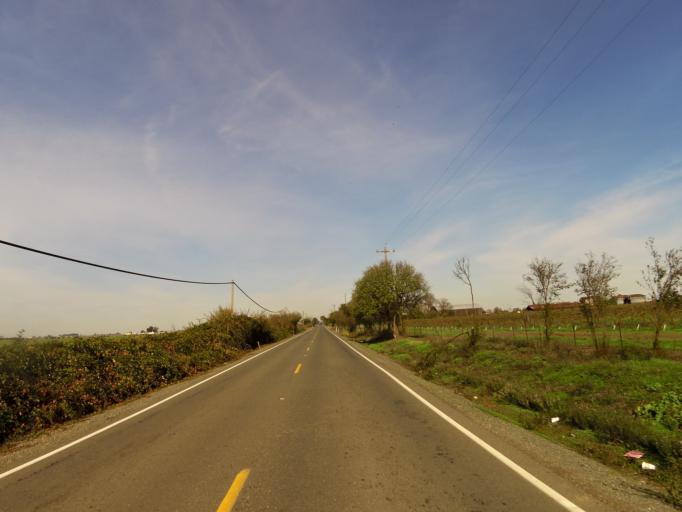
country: US
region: California
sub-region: San Joaquin County
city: Thornton
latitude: 38.2922
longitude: -121.4199
